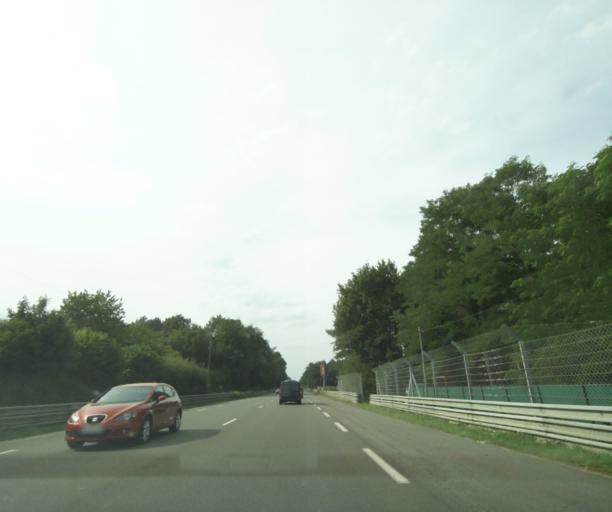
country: FR
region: Pays de la Loire
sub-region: Departement de la Sarthe
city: Mulsanne
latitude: 47.9320
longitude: 0.2396
